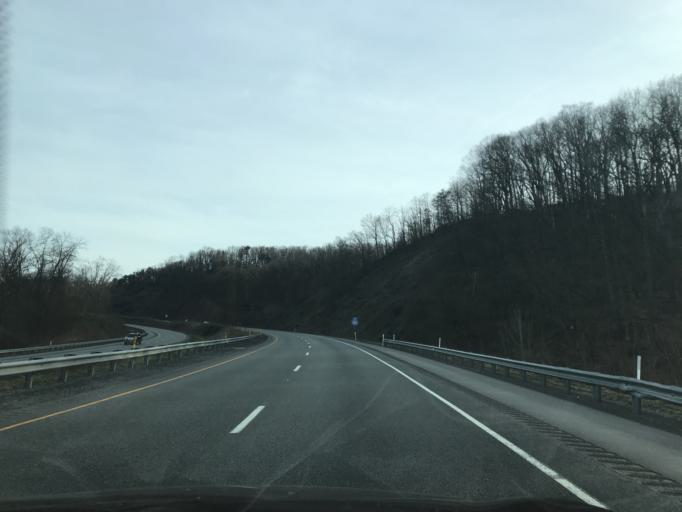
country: US
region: Pennsylvania
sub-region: Lycoming County
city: Muncy
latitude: 41.1822
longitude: -76.7926
